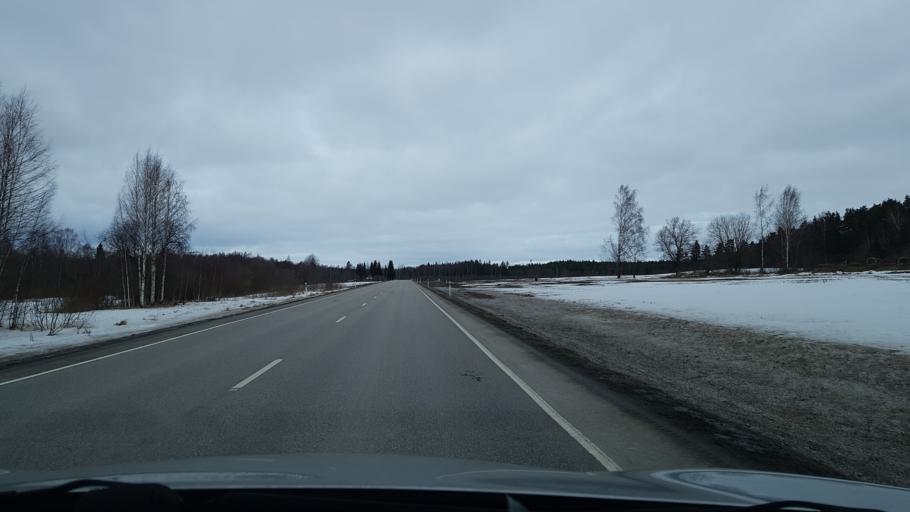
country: EE
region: Jogevamaa
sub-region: Tabivere vald
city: Tabivere
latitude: 58.6099
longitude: 26.5818
